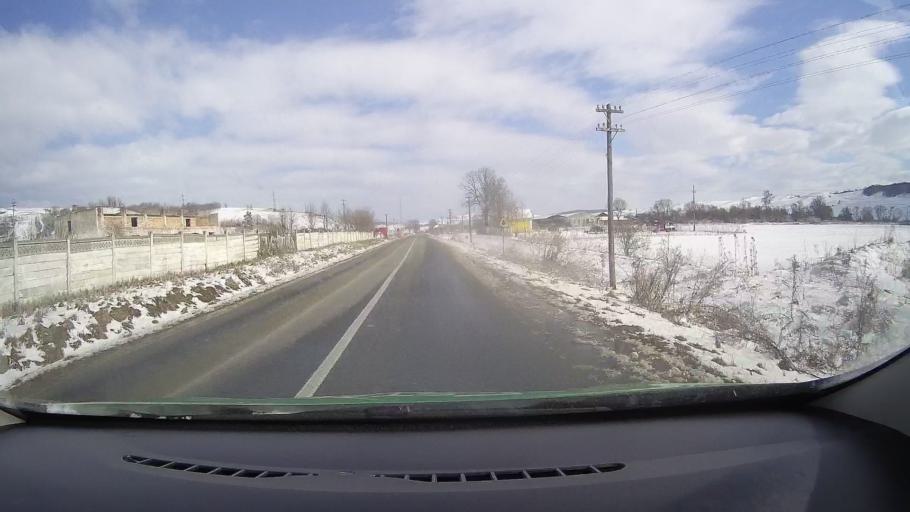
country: RO
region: Sibiu
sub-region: Oras Agnita
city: Agnita
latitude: 45.9643
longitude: 24.5833
